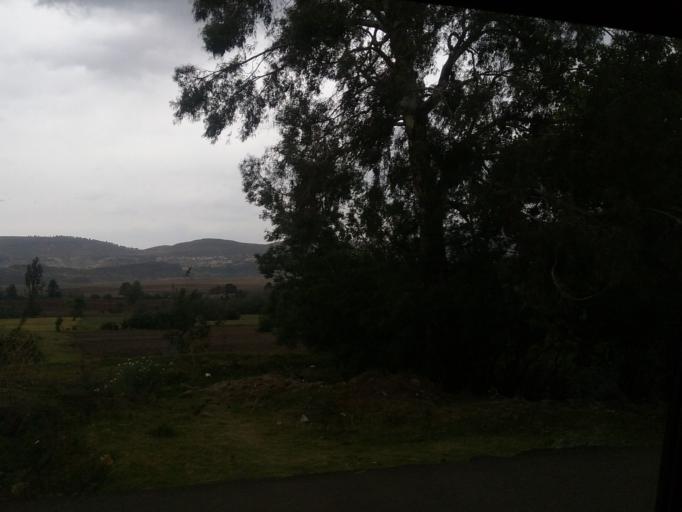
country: LS
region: Maseru
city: Nako
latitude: -29.4630
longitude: 27.7274
